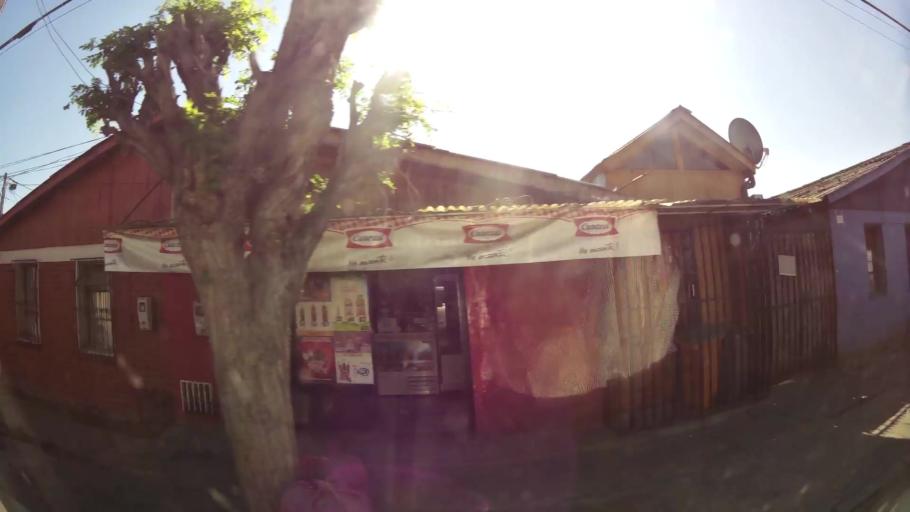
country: CL
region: Santiago Metropolitan
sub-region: Provincia de Maipo
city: San Bernardo
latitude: -33.5169
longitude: -70.6993
